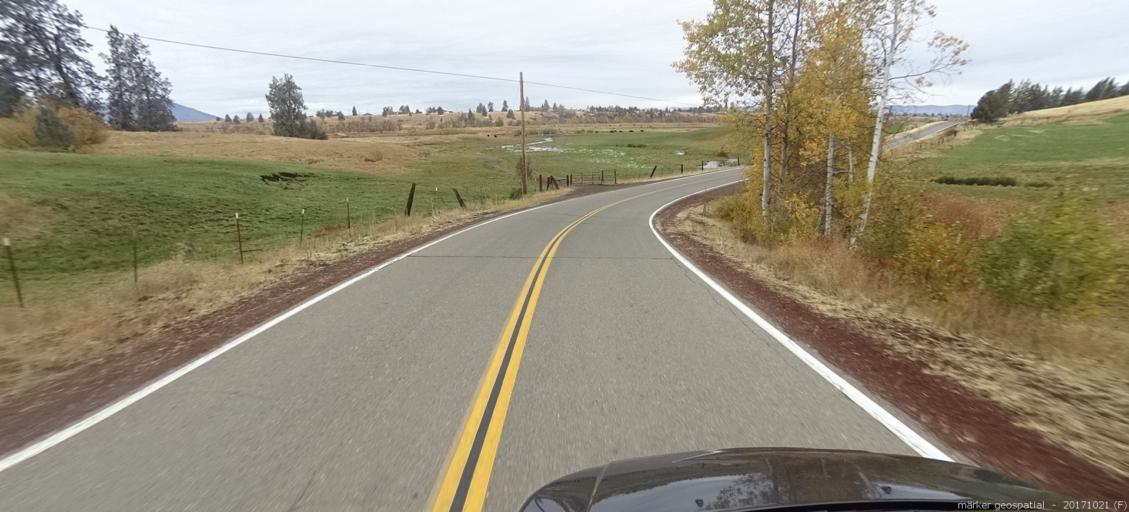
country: US
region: California
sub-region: Shasta County
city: Burney
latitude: 41.0101
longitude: -121.4217
